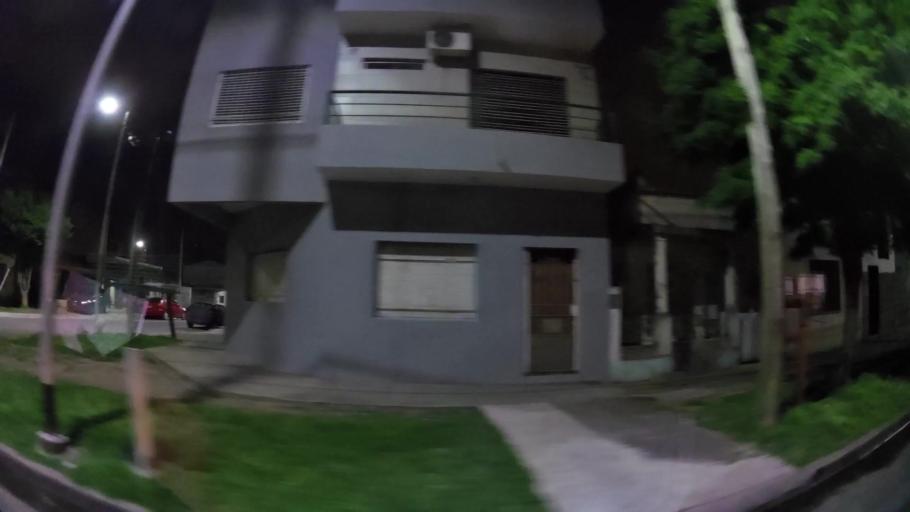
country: AR
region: Buenos Aires
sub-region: Partido de Avellaneda
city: Avellaneda
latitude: -34.7111
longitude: -58.3245
